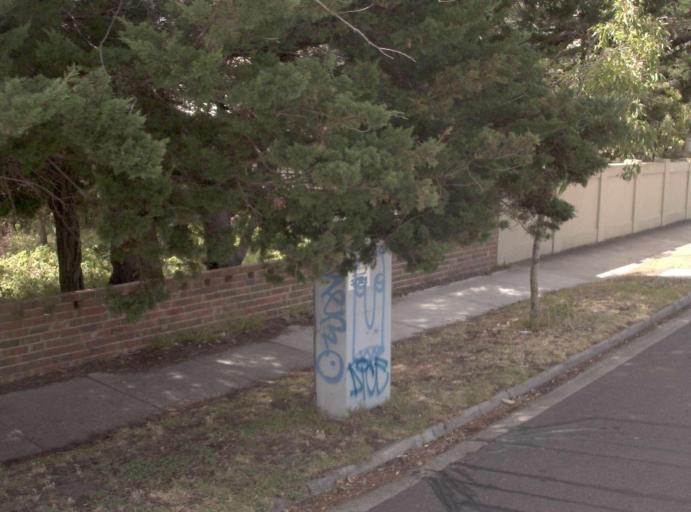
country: AU
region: Victoria
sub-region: Frankston
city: Seaford
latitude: -38.1126
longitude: 145.1257
